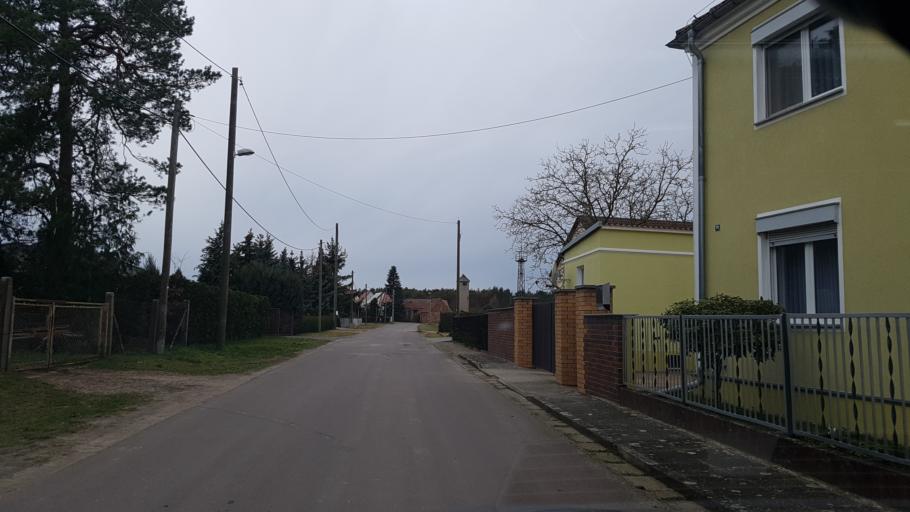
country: DE
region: Brandenburg
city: Bad Liebenwerda
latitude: 51.4941
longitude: 13.4032
